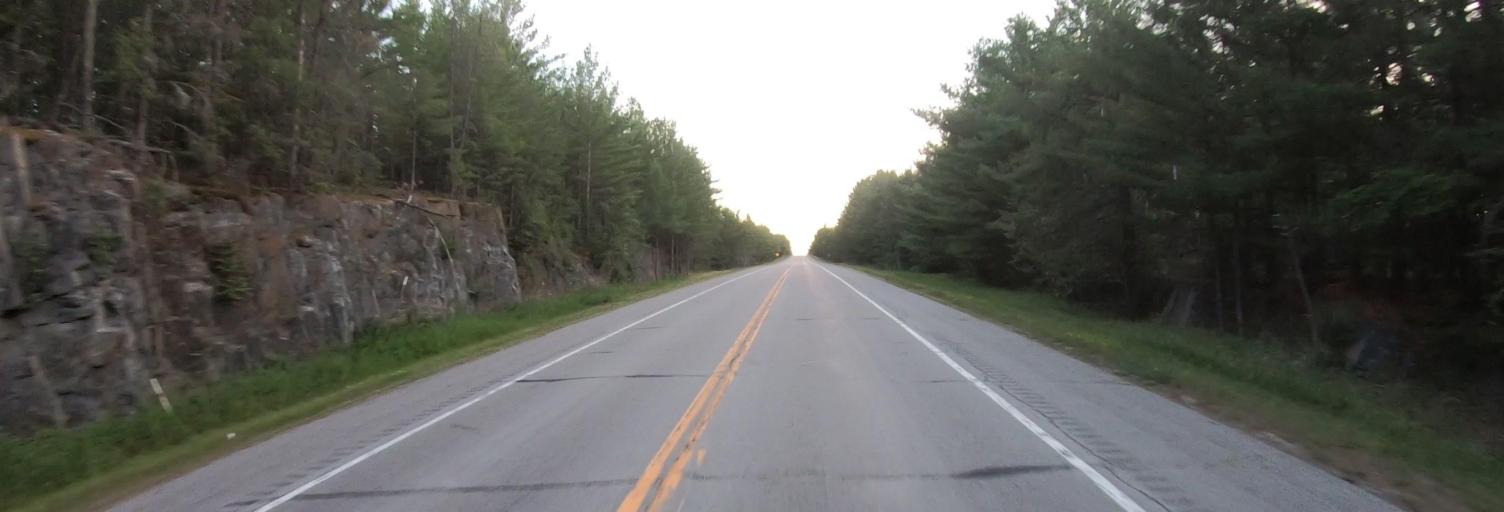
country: US
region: Minnesota
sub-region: Saint Louis County
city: Aurora
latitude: 47.7923
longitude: -92.3456
